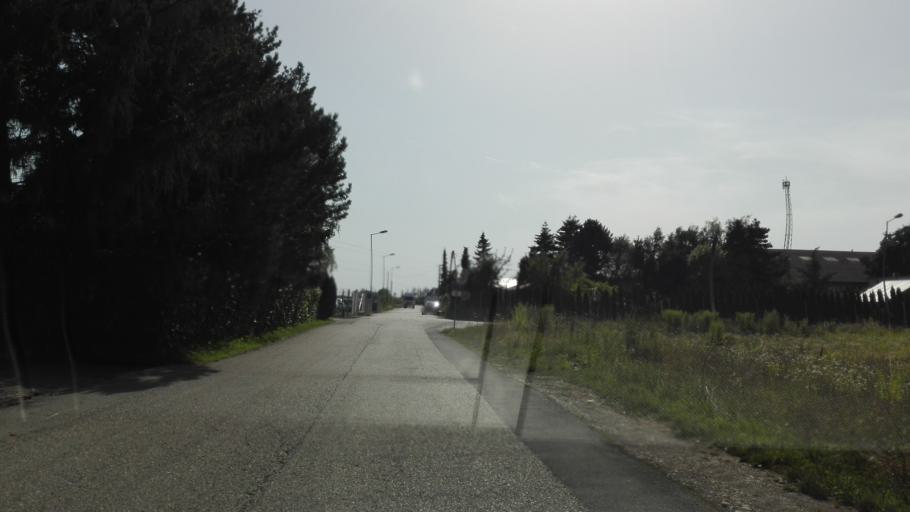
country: AT
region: Upper Austria
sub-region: Politischer Bezirk Linz-Land
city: Horsching
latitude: 48.2062
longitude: 14.1613
